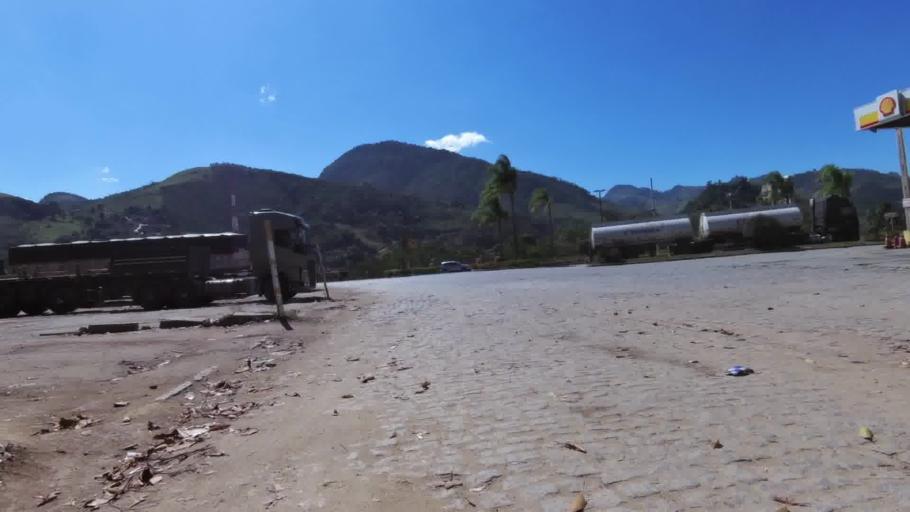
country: BR
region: Espirito Santo
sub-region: Rio Novo Do Sul
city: Rio Novo do Sul
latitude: -20.8667
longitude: -40.9322
